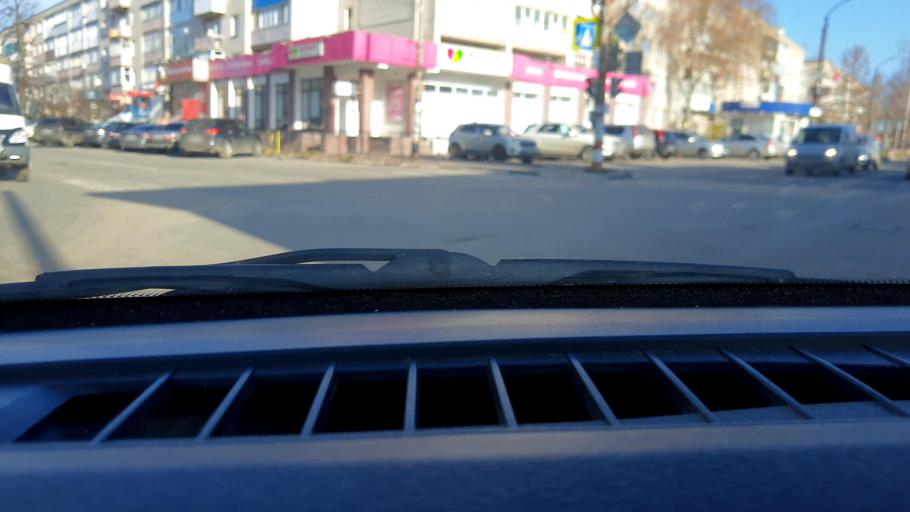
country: RU
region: Nizjnij Novgorod
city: Gorodets
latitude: 56.6448
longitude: 43.4722
